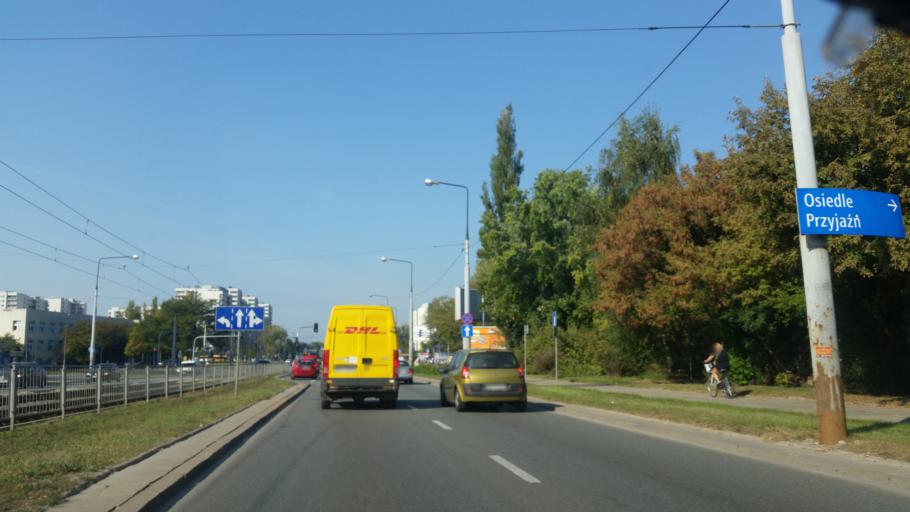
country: PL
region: Masovian Voivodeship
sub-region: Warszawa
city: Bemowo
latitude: 52.2359
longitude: 20.9143
